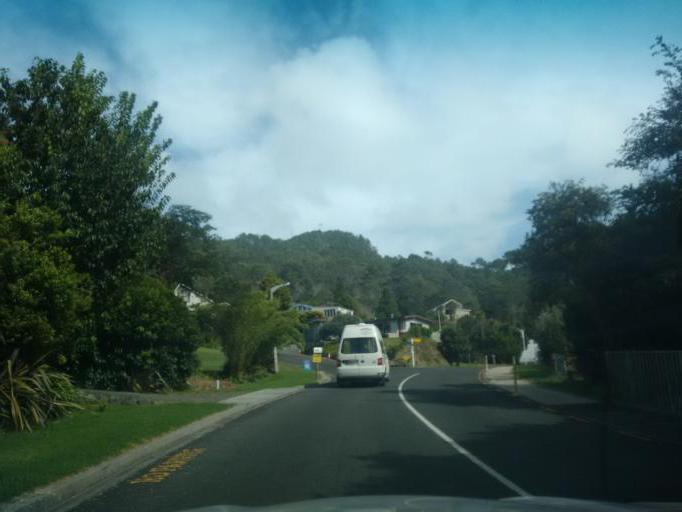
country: NZ
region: Waikato
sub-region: Thames-Coromandel District
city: Whitianga
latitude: -36.8398
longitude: 175.7992
